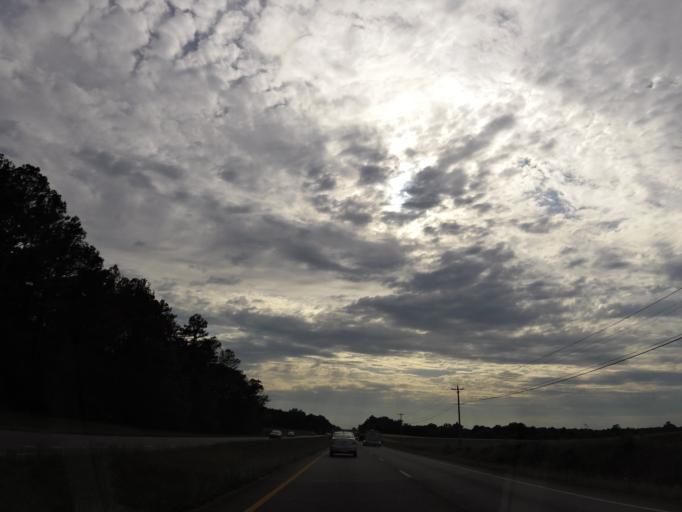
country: US
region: Alabama
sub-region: Morgan County
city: Decatur
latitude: 34.6282
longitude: -86.9166
